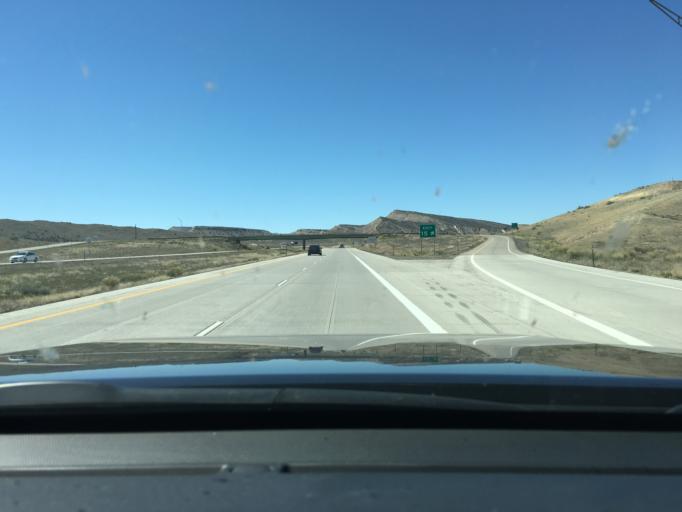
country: US
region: Colorado
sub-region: Mesa County
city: Loma
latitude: 39.1781
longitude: -108.8096
